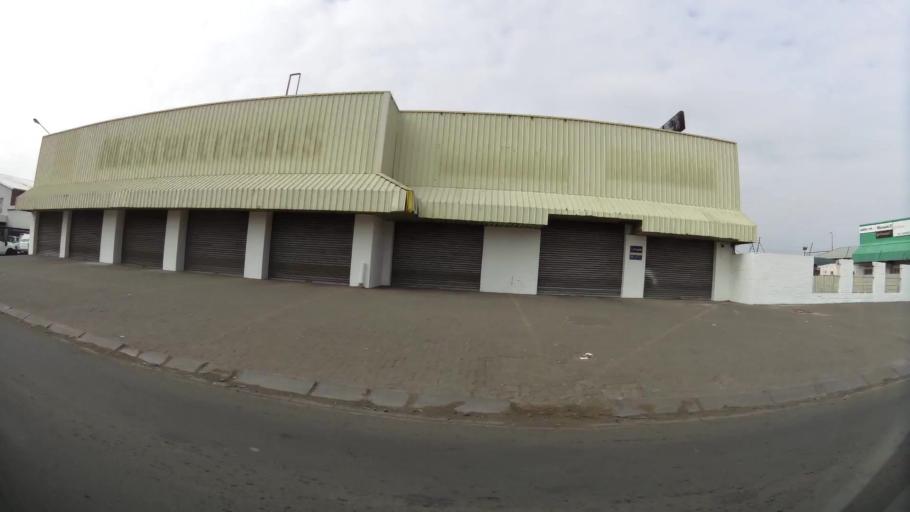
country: ZA
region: Orange Free State
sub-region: Mangaung Metropolitan Municipality
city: Bloemfontein
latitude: -29.1321
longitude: 26.2214
